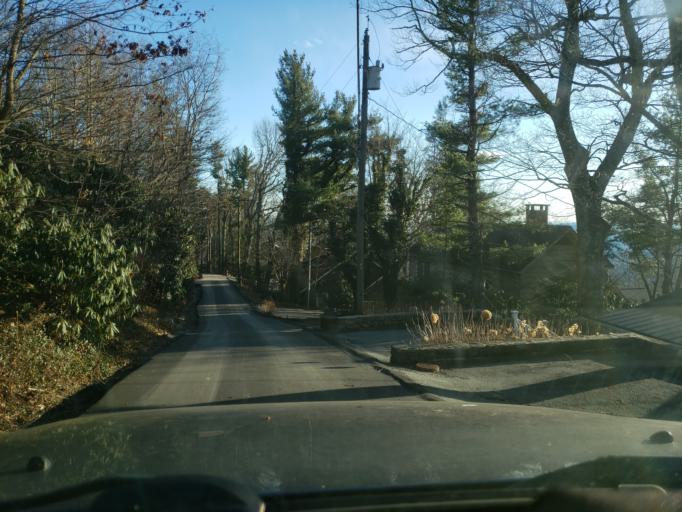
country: US
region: North Carolina
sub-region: Watauga County
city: Blowing Rock
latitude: 36.1235
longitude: -81.6777
